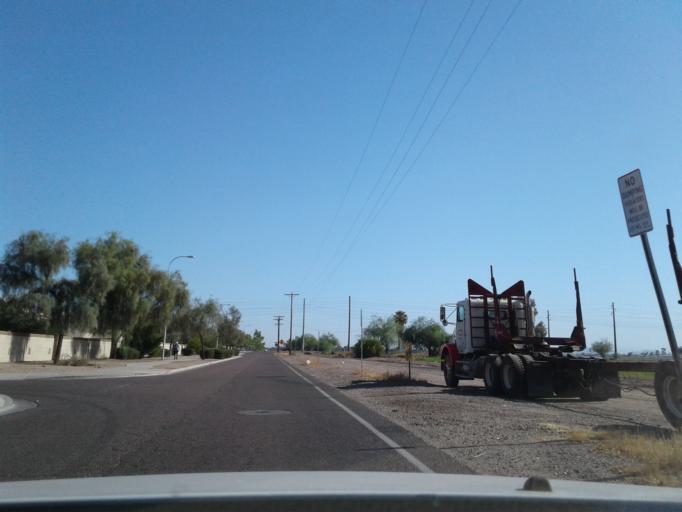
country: US
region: Arizona
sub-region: Maricopa County
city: Laveen
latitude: 33.4208
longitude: -112.1953
